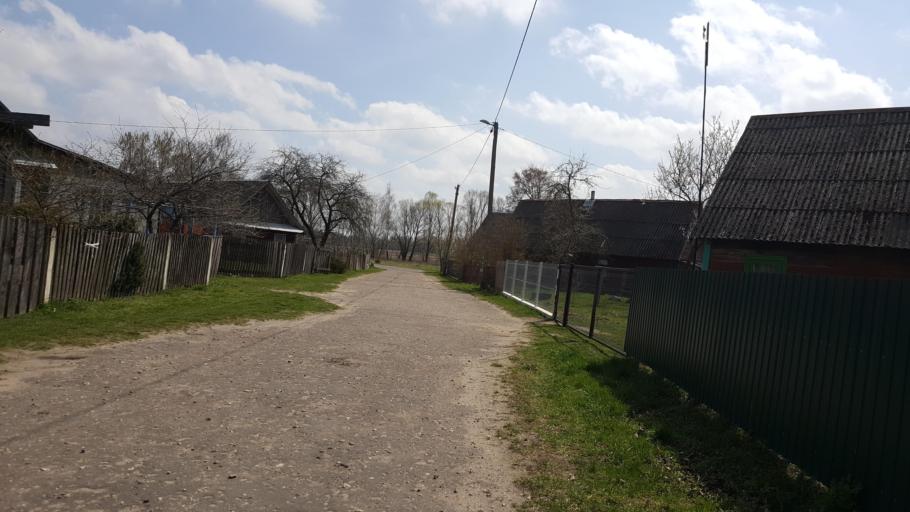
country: BY
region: Brest
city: Zhabinka
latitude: 52.2531
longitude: 23.9646
